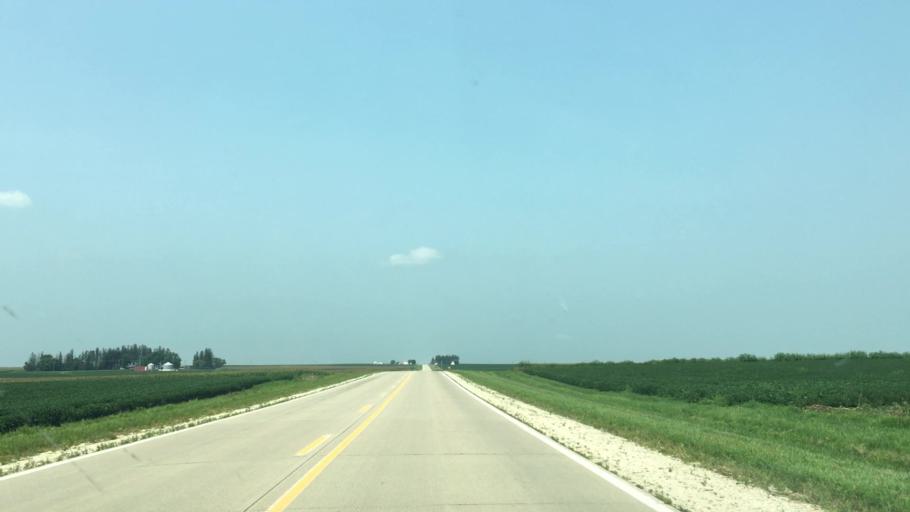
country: US
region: Iowa
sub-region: Fayette County
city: Oelwein
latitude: 42.6935
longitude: -91.8051
